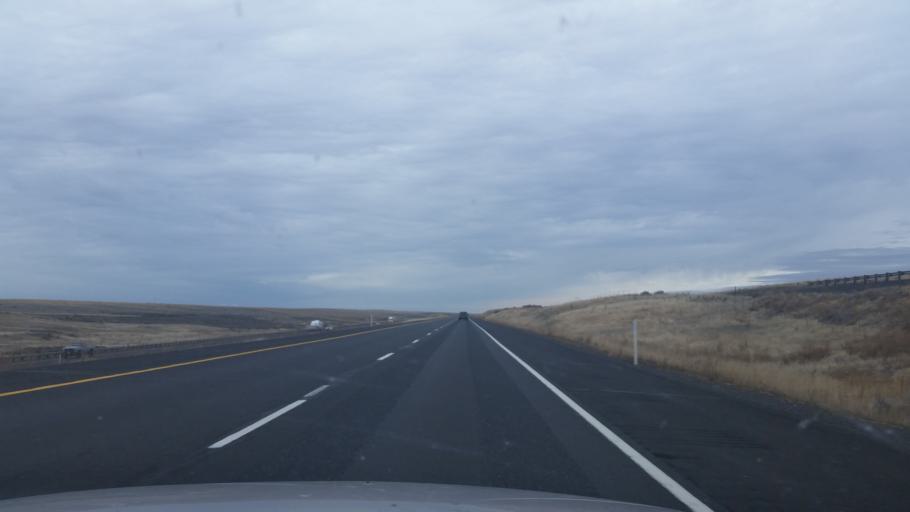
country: US
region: Washington
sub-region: Adams County
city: Ritzville
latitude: 47.1078
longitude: -118.5846
